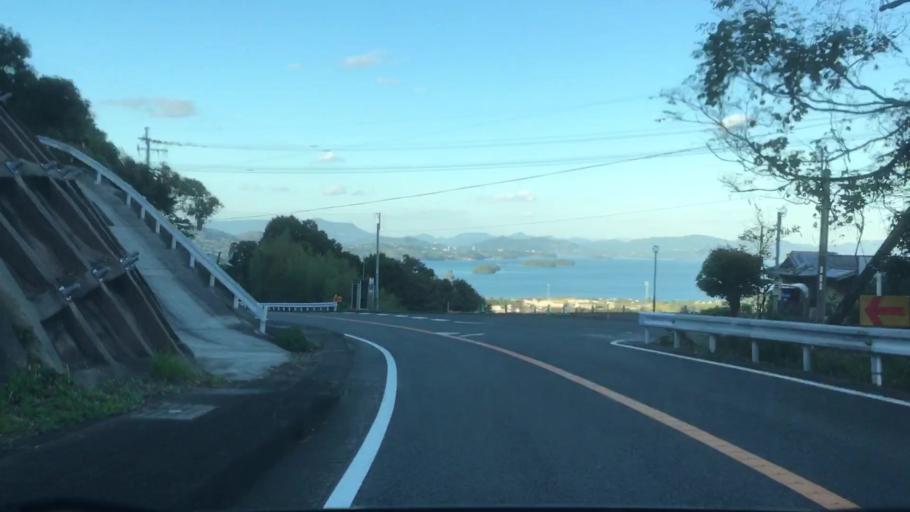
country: JP
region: Nagasaki
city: Sasebo
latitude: 32.9913
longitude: 129.7242
